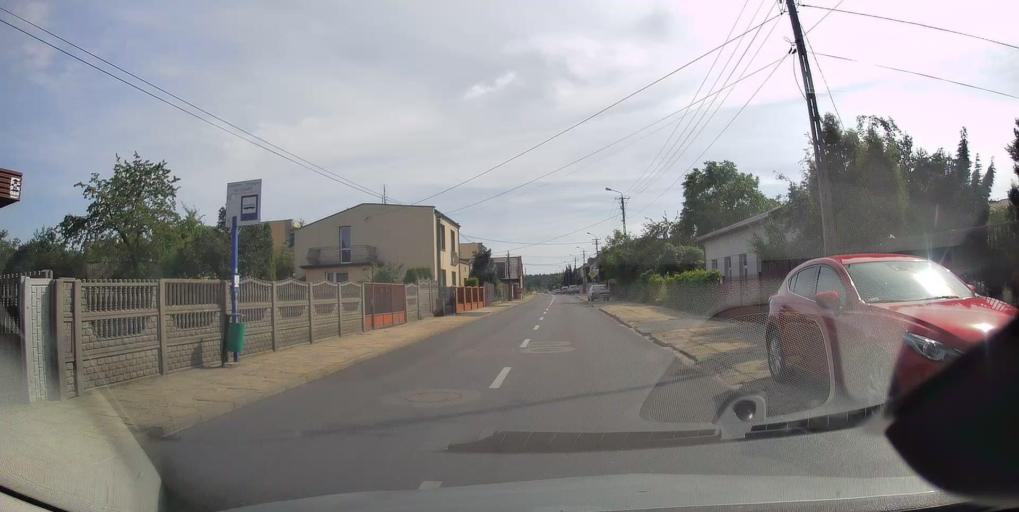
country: PL
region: Lodz Voivodeship
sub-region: Powiat tomaszowski
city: Tomaszow Mazowiecki
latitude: 51.5242
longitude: 19.9976
